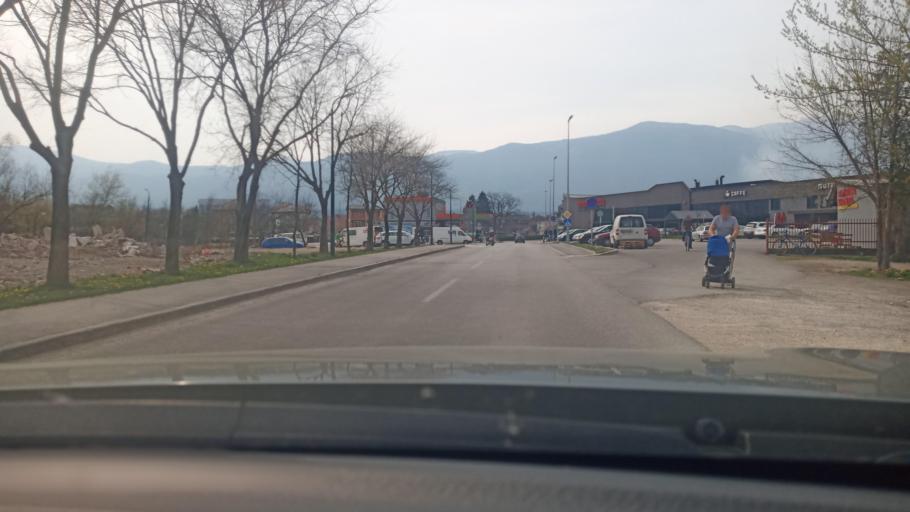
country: BA
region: Federation of Bosnia and Herzegovina
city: Bihac
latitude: 44.8216
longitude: 15.8635
